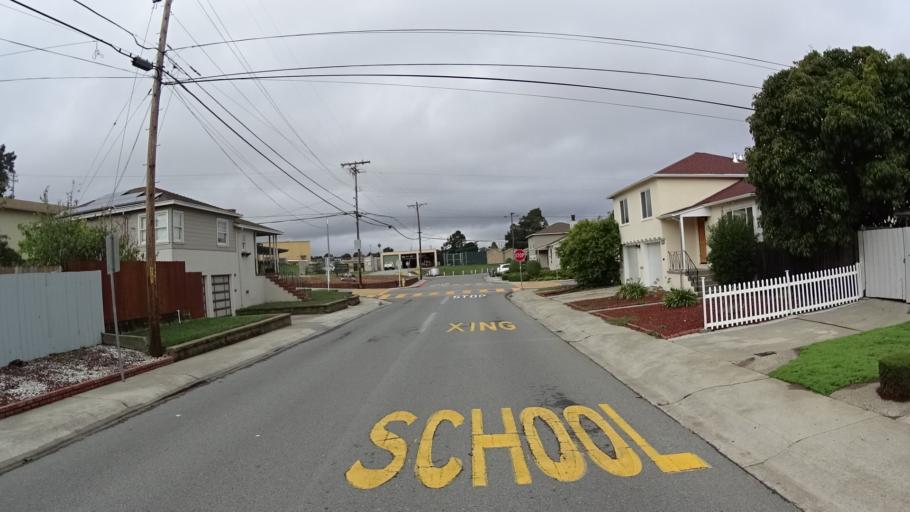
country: US
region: California
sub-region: San Mateo County
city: Millbrae
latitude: 37.6090
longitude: -122.4034
